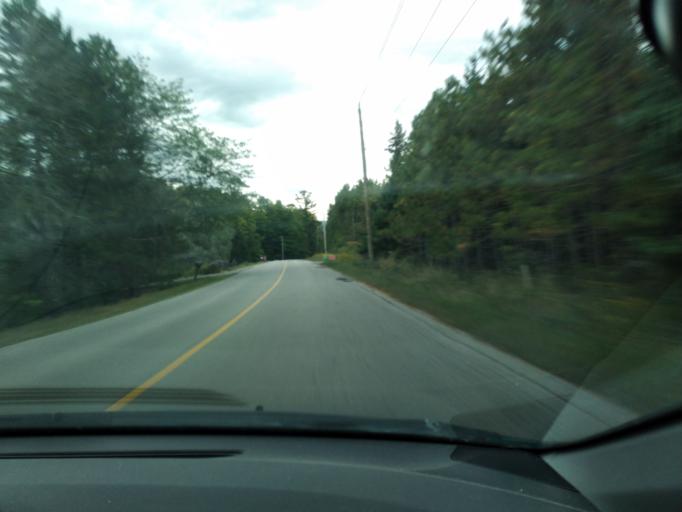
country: CA
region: Ontario
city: Bradford West Gwillimbury
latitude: 43.9521
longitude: -79.7783
